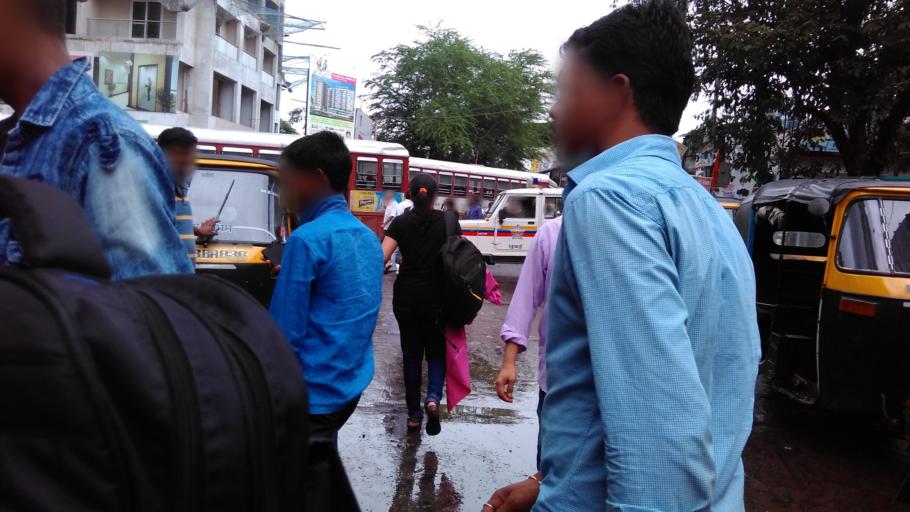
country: IN
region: Maharashtra
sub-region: Mumbai Suburban
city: Mumbai
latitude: 19.0648
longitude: 72.8809
